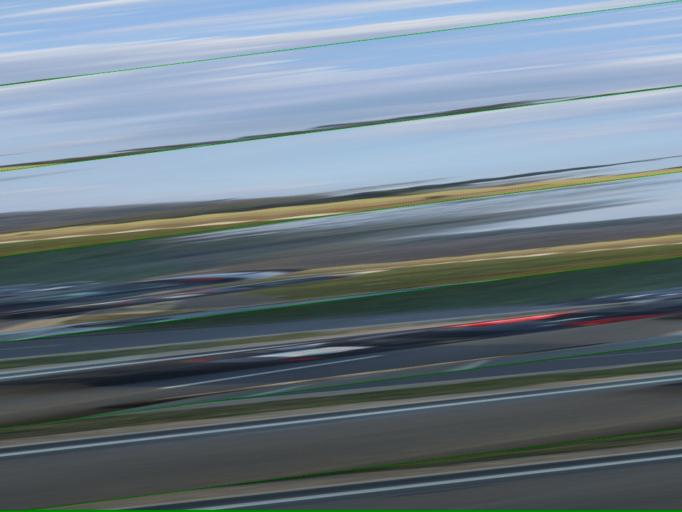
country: FR
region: Ile-de-France
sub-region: Departement des Yvelines
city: Plaisir
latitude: 48.8081
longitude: 1.9593
